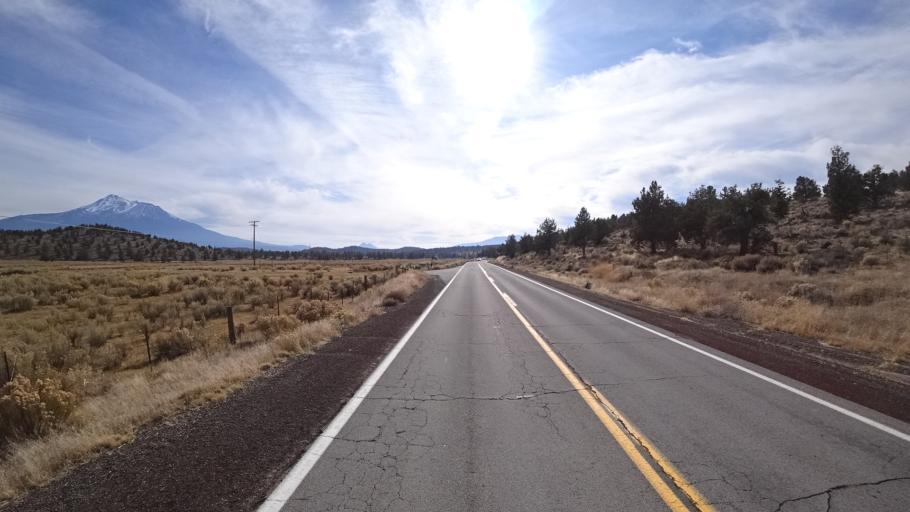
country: US
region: California
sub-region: Siskiyou County
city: Weed
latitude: 41.5647
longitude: -122.3865
